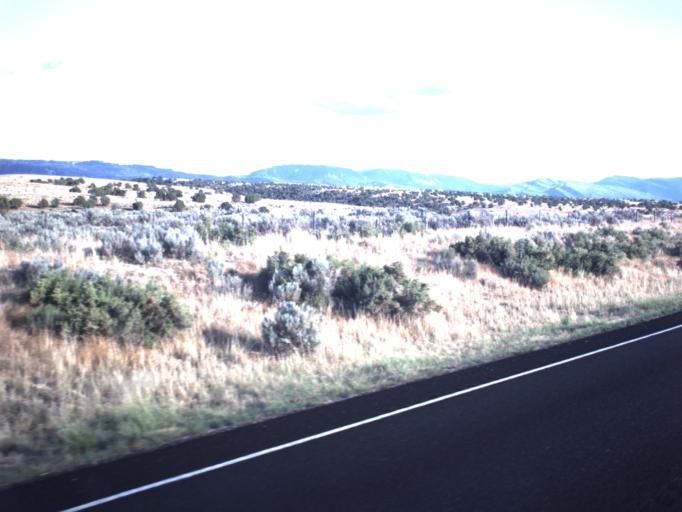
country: US
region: Utah
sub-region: Sanpete County
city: Moroni
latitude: 39.4488
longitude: -111.5447
